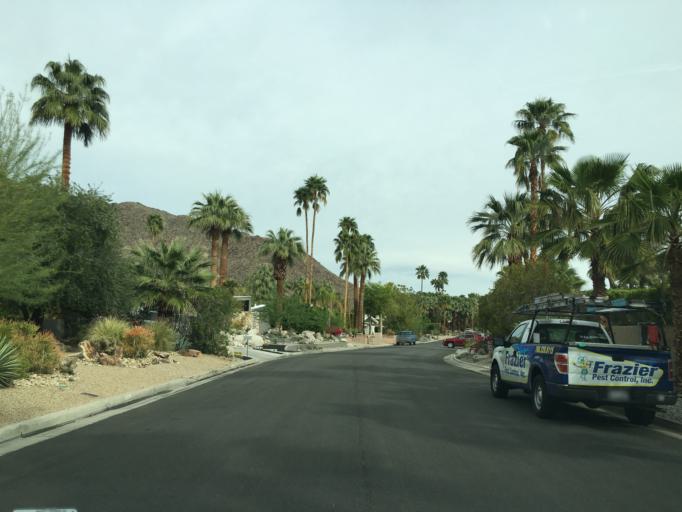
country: US
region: California
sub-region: Riverside County
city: Palm Springs
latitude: 33.8356
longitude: -116.5581
